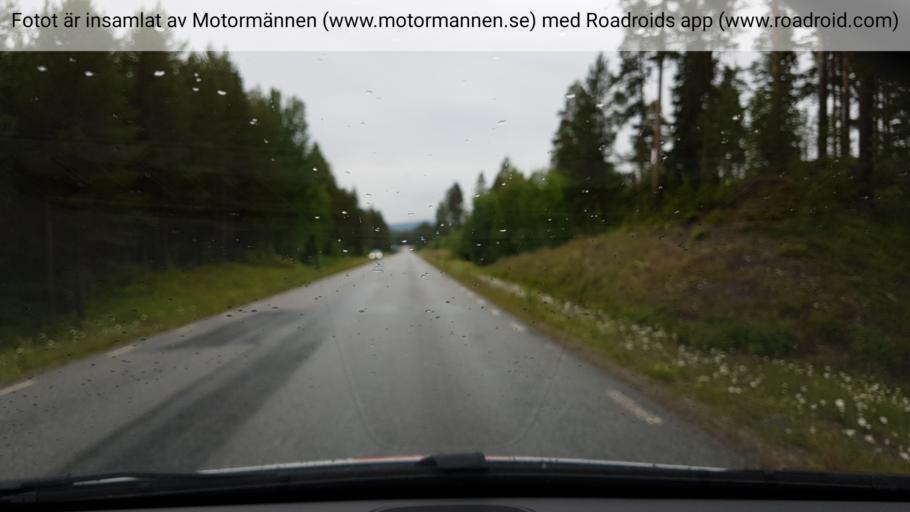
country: SE
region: Vaesterbotten
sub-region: Dorotea Kommun
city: Dorotea
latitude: 64.1490
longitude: 16.0538
